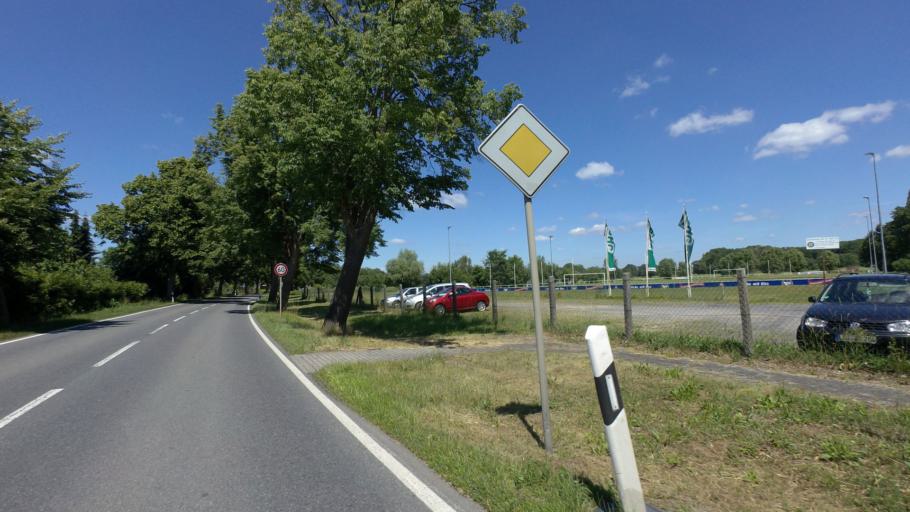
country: DE
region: Brandenburg
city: Golssen
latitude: 51.9644
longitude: 13.6170
